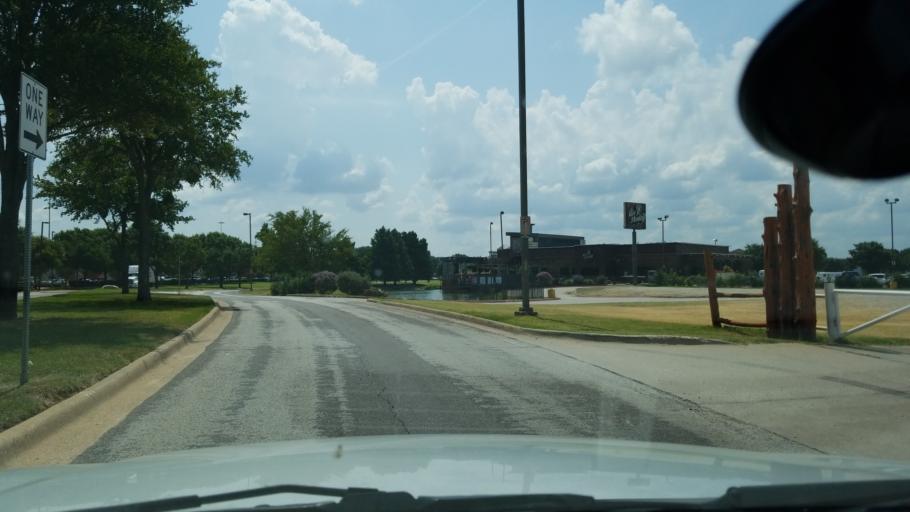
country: US
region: Texas
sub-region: Dallas County
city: Farmers Branch
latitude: 32.8619
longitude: -96.8968
